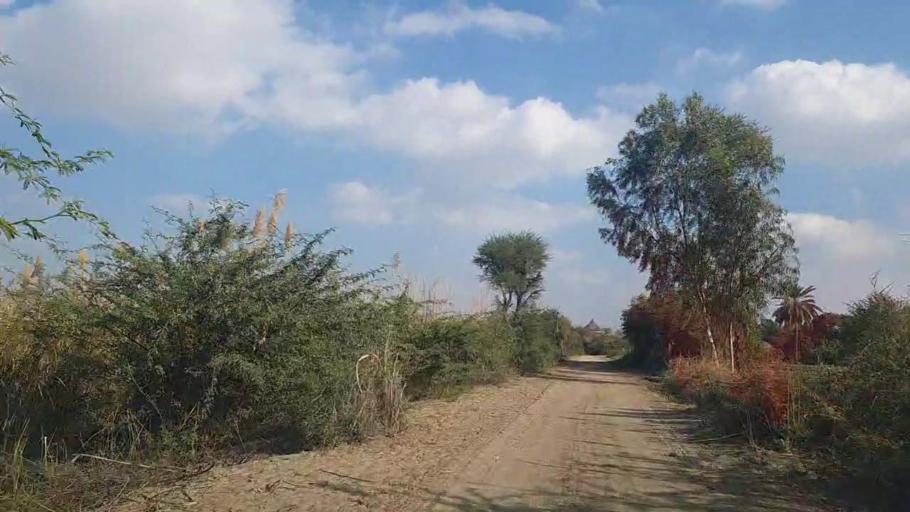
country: PK
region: Sindh
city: Tando Mittha Khan
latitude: 25.9893
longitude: 69.2451
